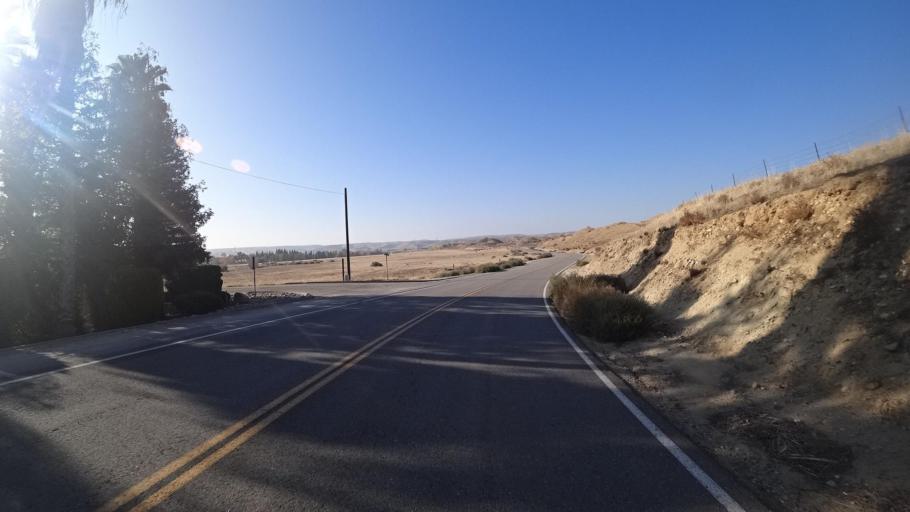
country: US
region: California
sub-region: Kern County
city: Oildale
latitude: 35.4488
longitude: -118.9217
